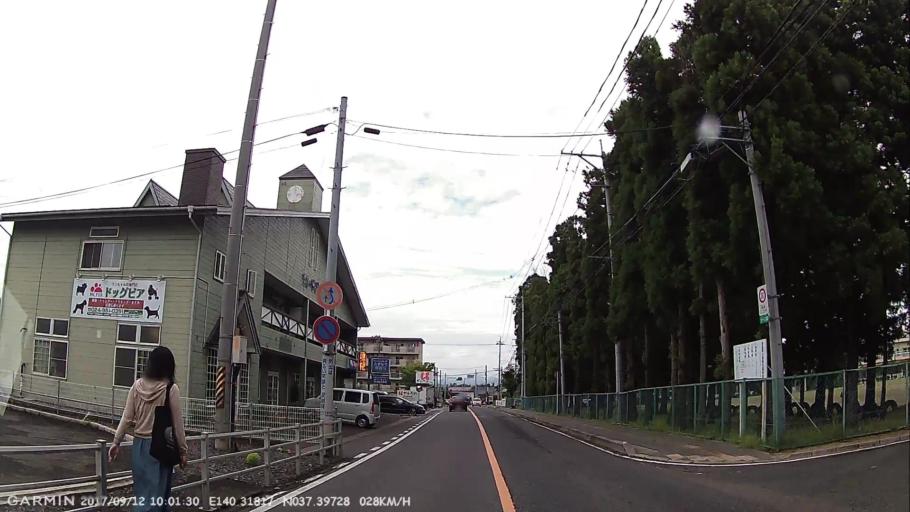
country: JP
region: Fukushima
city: Koriyama
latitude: 37.3973
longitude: 140.3181
